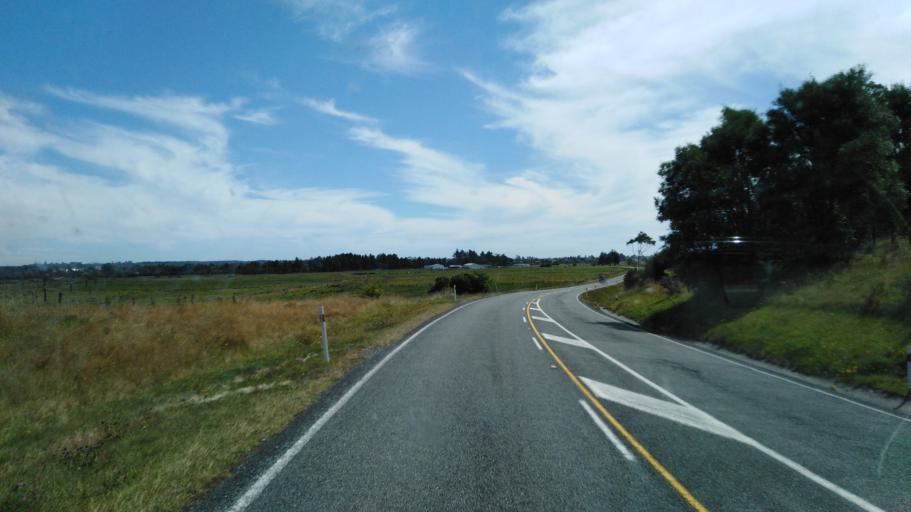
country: NZ
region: West Coast
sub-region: Buller District
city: Westport
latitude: -41.7594
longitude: 171.6448
